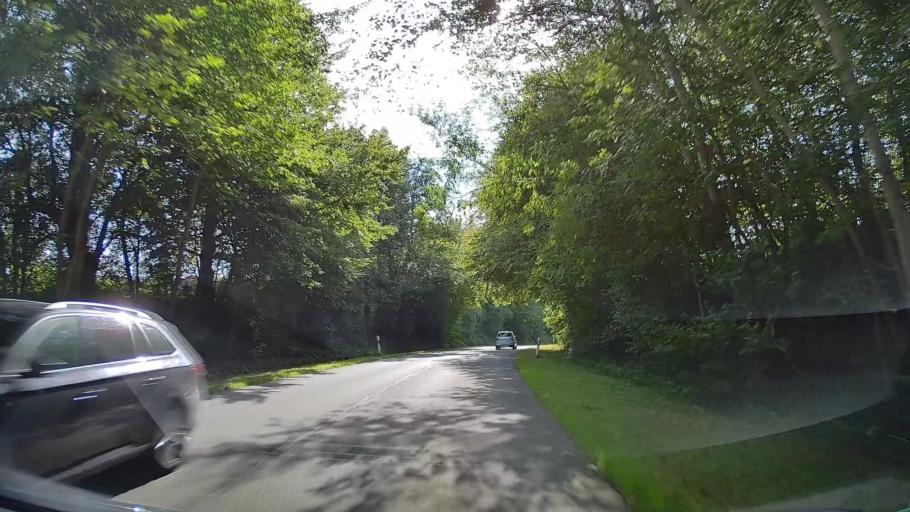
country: DE
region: Schleswig-Holstein
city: Glucksburg
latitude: 54.8459
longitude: 9.5857
